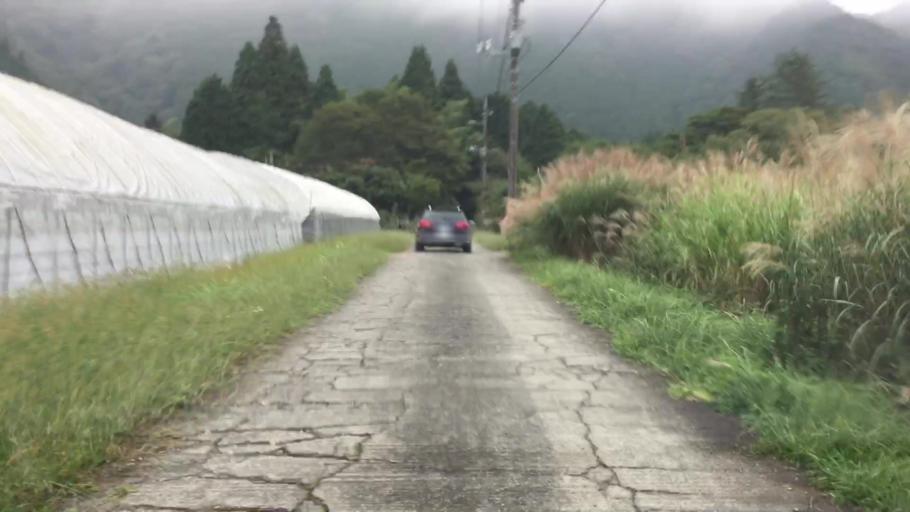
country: JP
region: Yamanashi
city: Fujikawaguchiko
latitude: 35.4043
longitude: 138.5663
